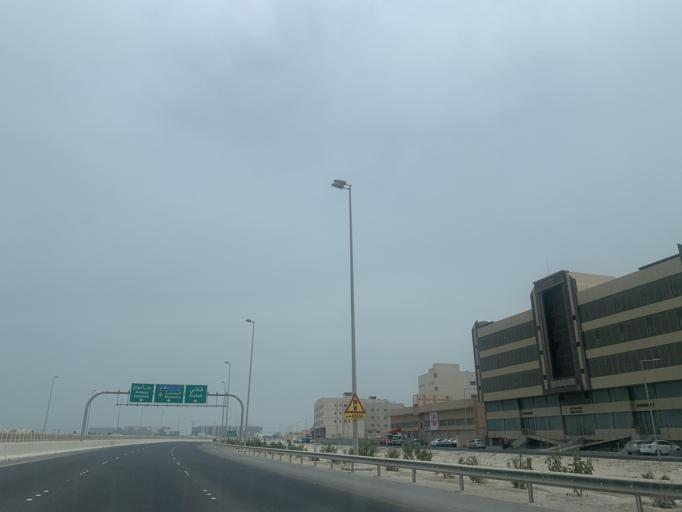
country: BH
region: Muharraq
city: Al Hadd
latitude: 26.2788
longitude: 50.6549
